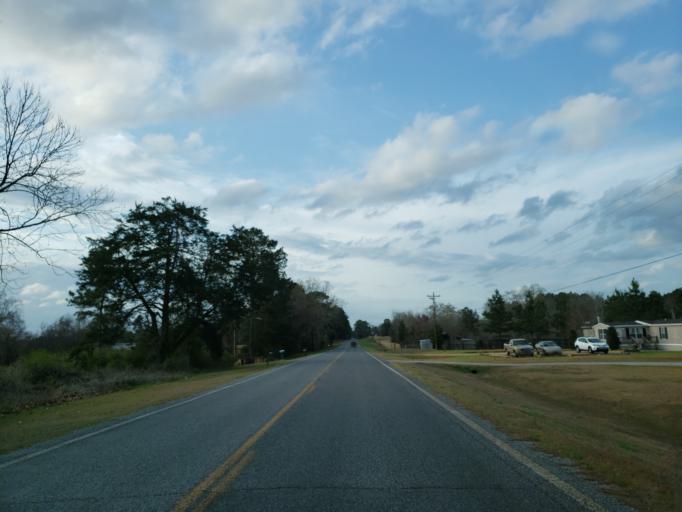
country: US
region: Mississippi
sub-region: Clarke County
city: Stonewall
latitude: 32.1854
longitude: -88.6780
